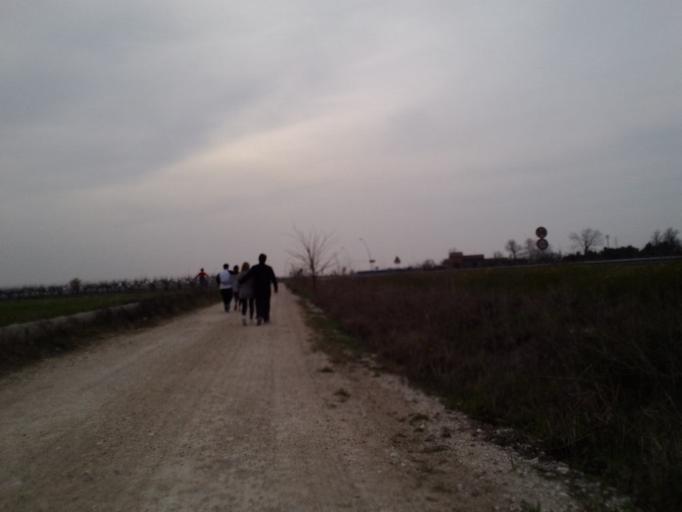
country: IT
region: Veneto
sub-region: Provincia di Verona
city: Povegliano Veronese
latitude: 45.3643
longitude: 10.8867
